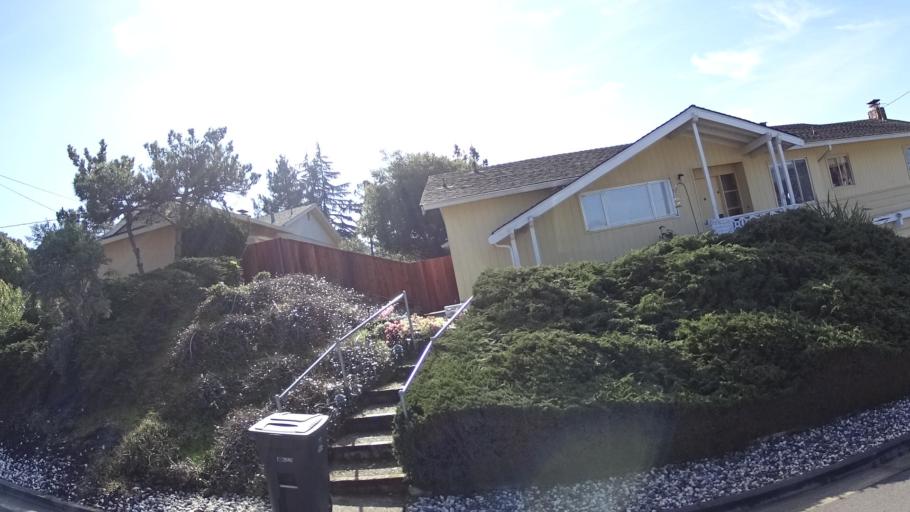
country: US
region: California
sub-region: Alameda County
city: Fairview
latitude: 37.6637
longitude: -122.0475
